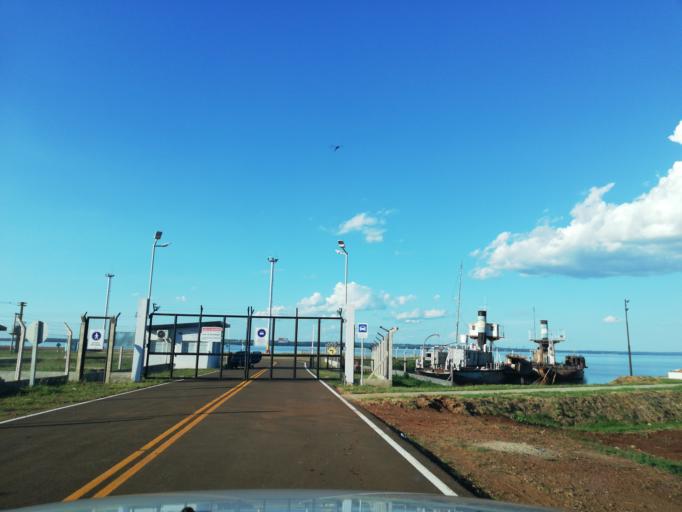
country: PY
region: Itapua
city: San Juan del Parana
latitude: -27.3693
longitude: -55.9845
